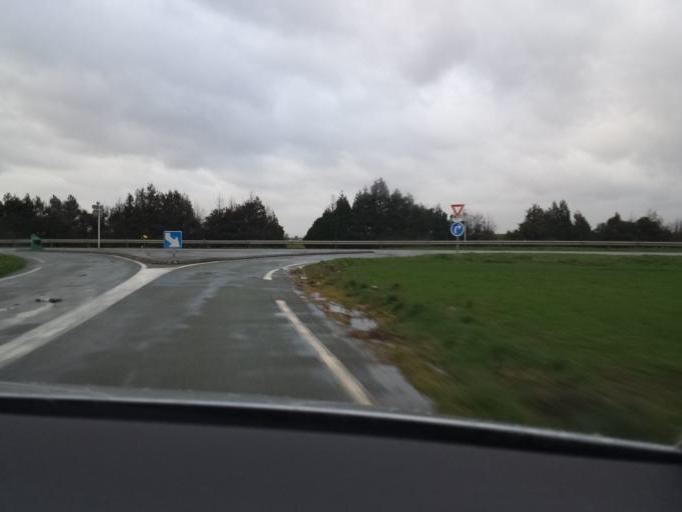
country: FR
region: Haute-Normandie
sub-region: Departement de l'Eure
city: Gravigny
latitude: 49.0141
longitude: 1.2136
